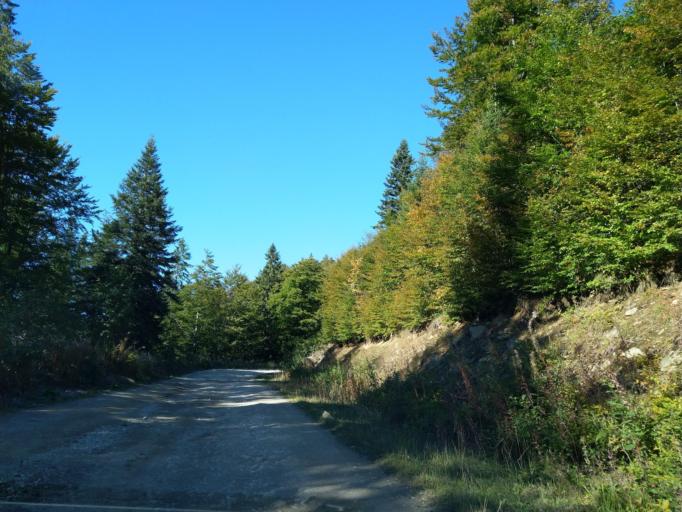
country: RS
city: Sokolovica
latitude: 43.3654
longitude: 20.2590
